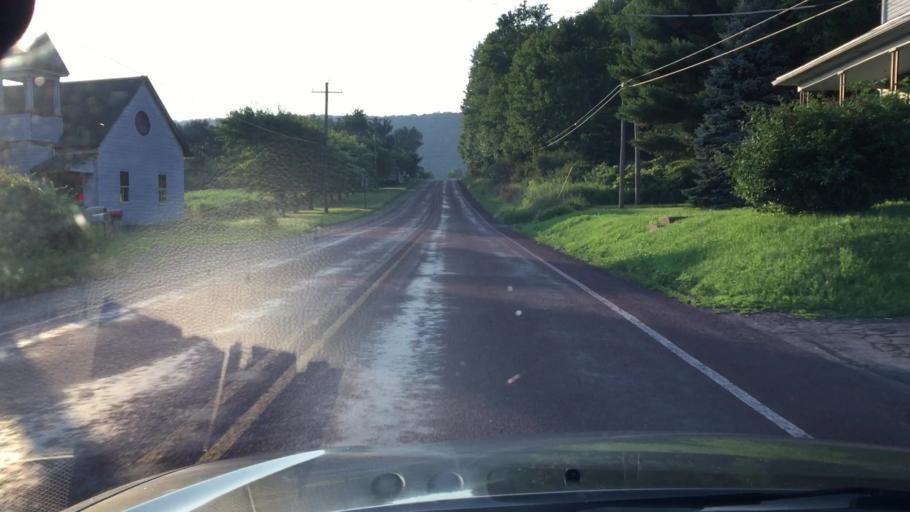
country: US
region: Pennsylvania
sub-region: Carbon County
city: Weatherly
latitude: 40.9220
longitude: -75.8623
